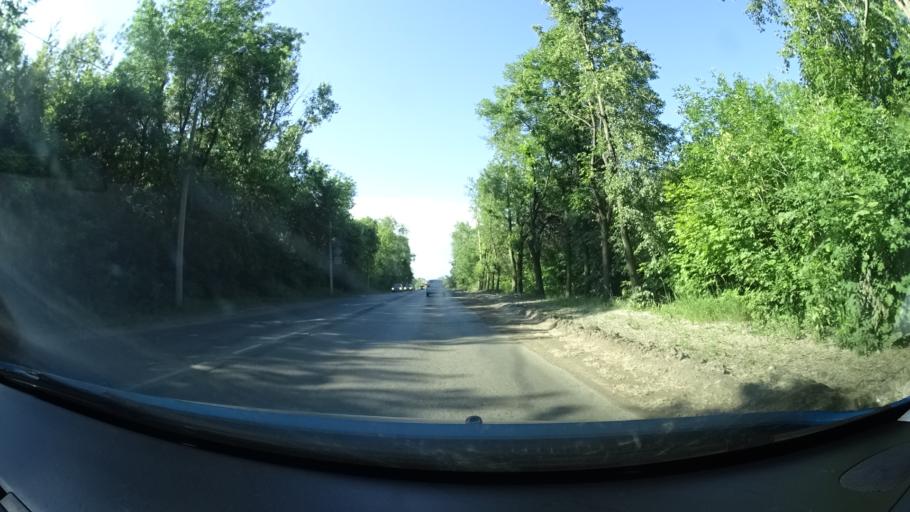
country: RU
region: Bashkortostan
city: Ufa
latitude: 54.8501
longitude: 56.0769
